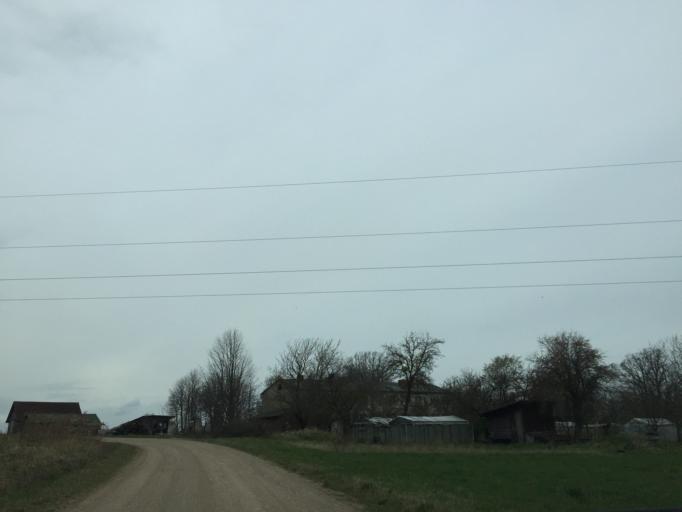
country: LV
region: Priekuli
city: Priekuli
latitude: 57.3376
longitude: 25.3717
